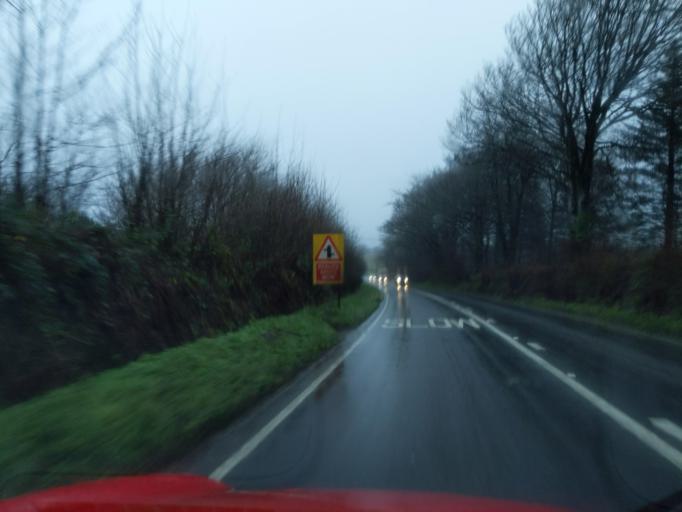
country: GB
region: England
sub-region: Cornwall
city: South Hill
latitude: 50.5280
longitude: -4.3256
